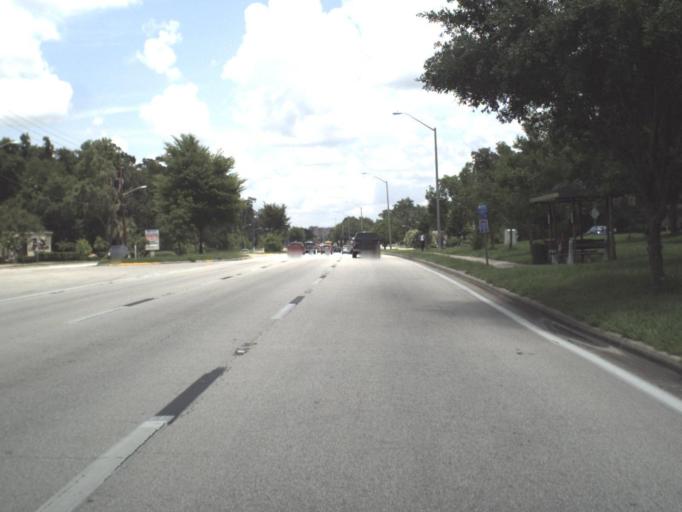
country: US
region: Florida
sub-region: Alachua County
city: Gainesville
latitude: 29.6289
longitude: -82.3686
